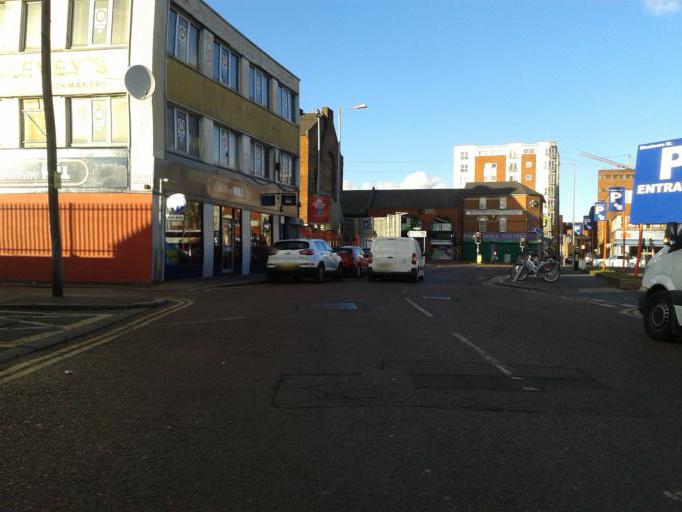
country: GB
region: Northern Ireland
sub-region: City of Belfast
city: Belfast
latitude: 54.6017
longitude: -5.9336
